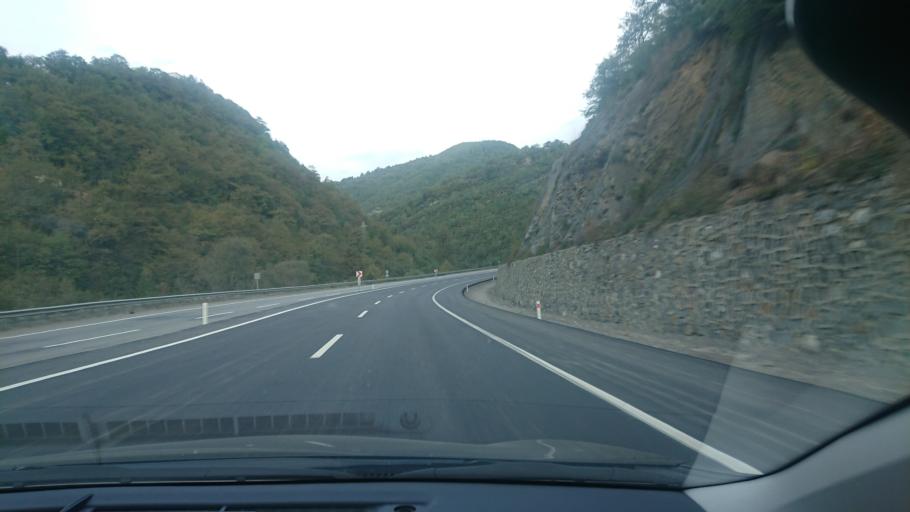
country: TR
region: Zonguldak
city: Beycuma
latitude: 41.3868
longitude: 31.9380
